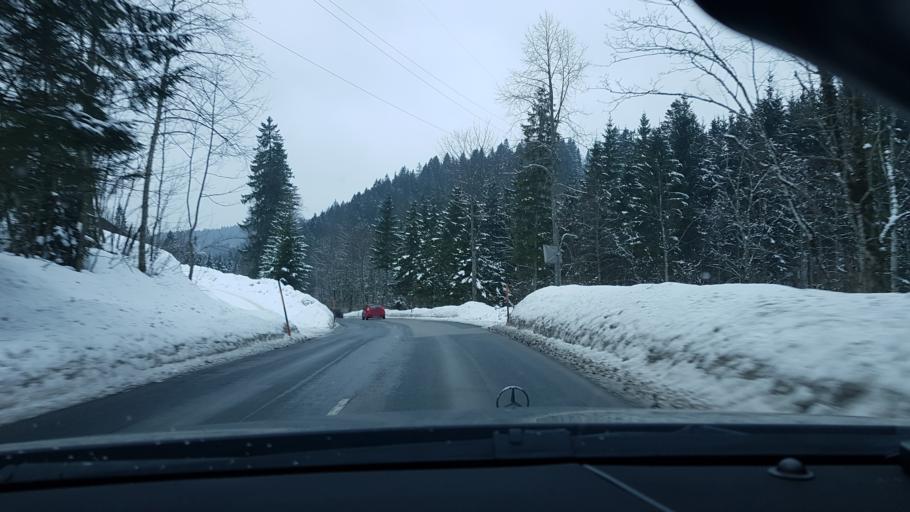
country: AT
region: Lower Austria
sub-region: Politischer Bezirk Scheibbs
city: Gaming
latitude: 47.8716
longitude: 15.1340
